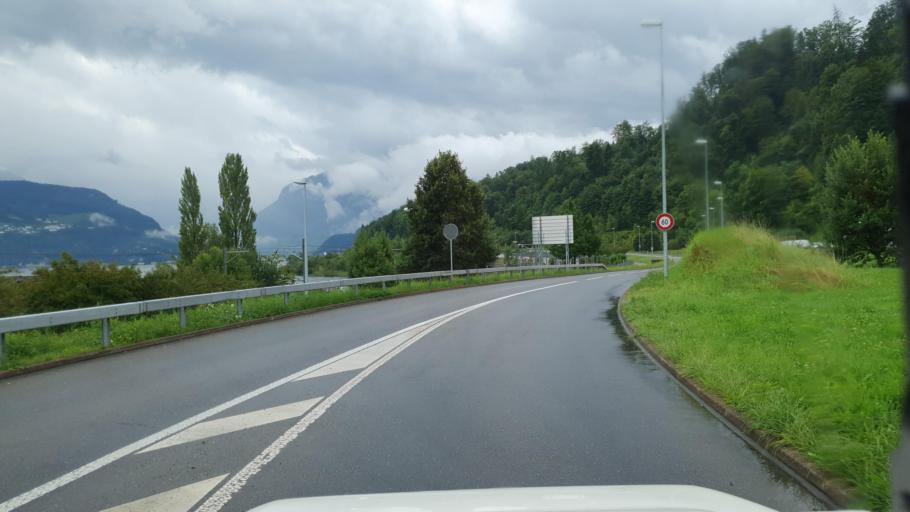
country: CH
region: Lucerne
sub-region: Lucerne-Land District
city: Horw
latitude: 47.0080
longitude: 8.3049
